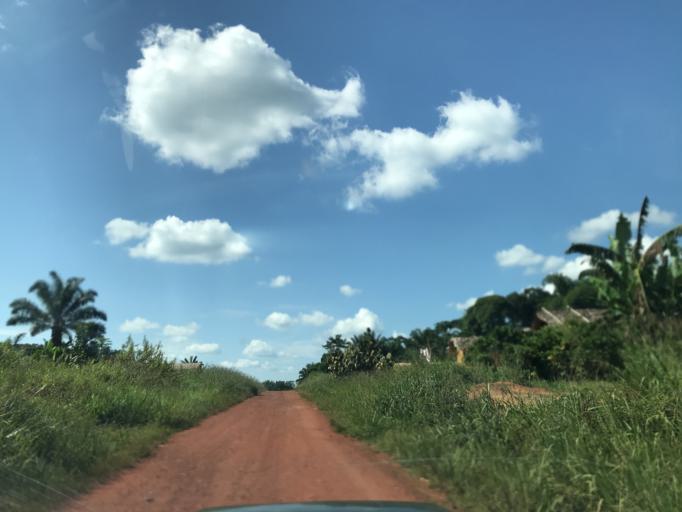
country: CD
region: Eastern Province
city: Kisangani
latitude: 1.2192
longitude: 25.2681
